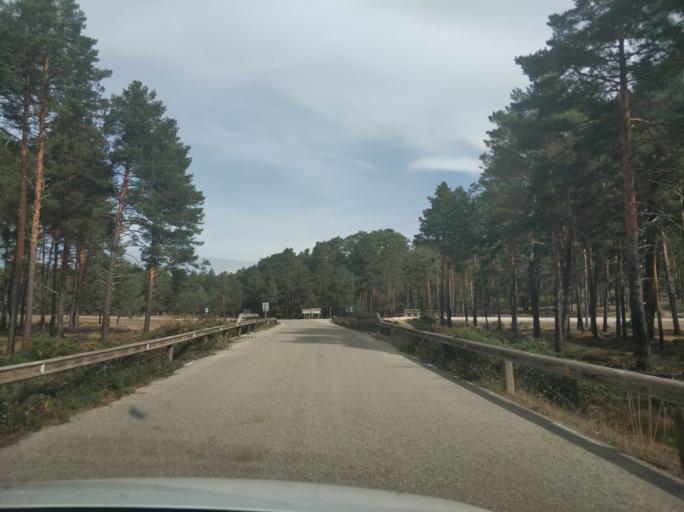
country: ES
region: Castille and Leon
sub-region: Provincia de Soria
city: Navaleno
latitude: 41.8653
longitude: -2.9427
